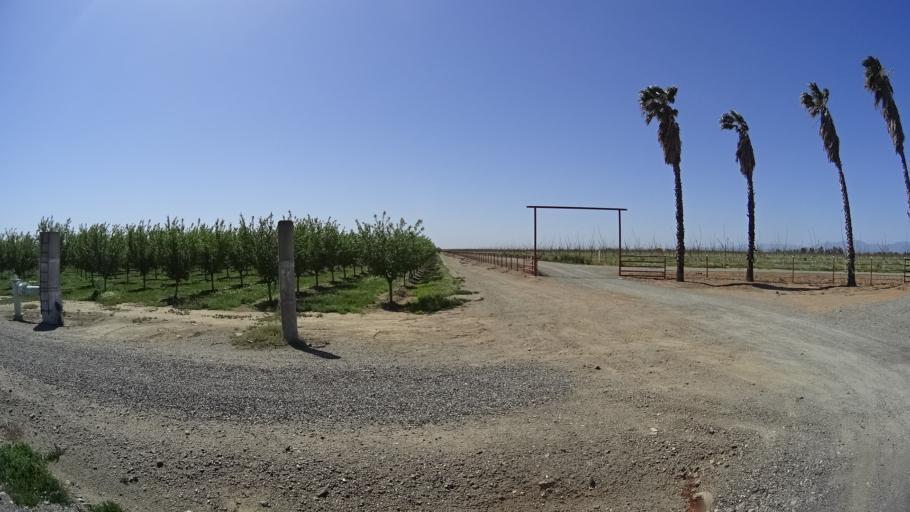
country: US
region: California
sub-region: Glenn County
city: Orland
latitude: 39.6965
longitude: -122.1685
